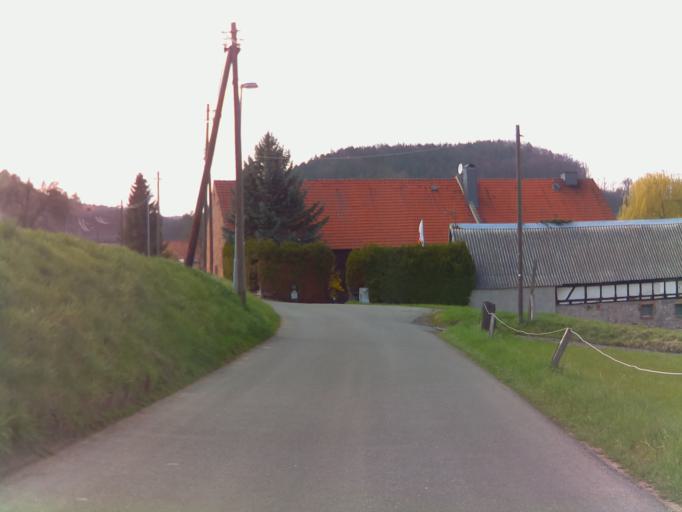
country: DE
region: Thuringia
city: Bibra
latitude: 50.8233
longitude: 11.5599
